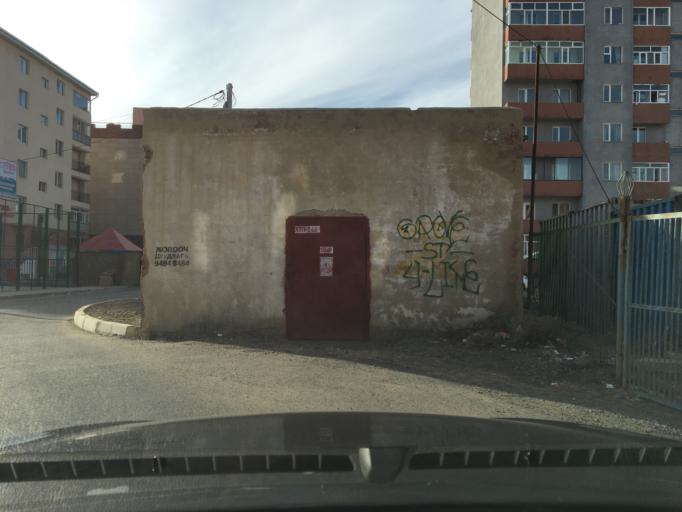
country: MN
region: Ulaanbaatar
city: Ulaanbaatar
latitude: 47.8948
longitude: 106.9171
